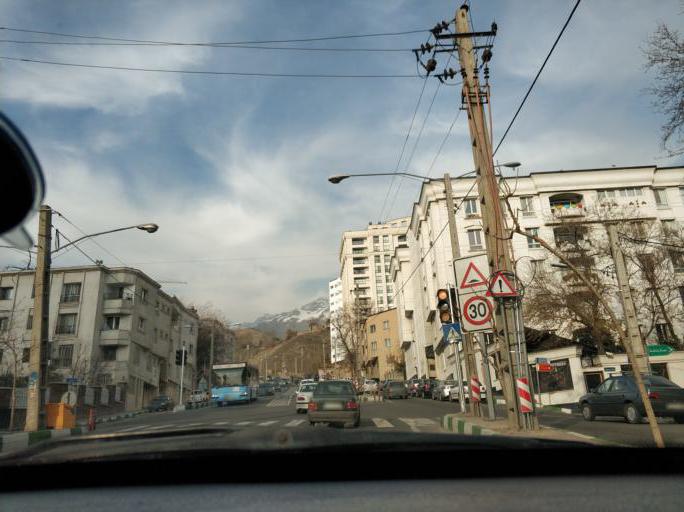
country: IR
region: Tehran
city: Tajrish
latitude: 35.8108
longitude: 51.4847
